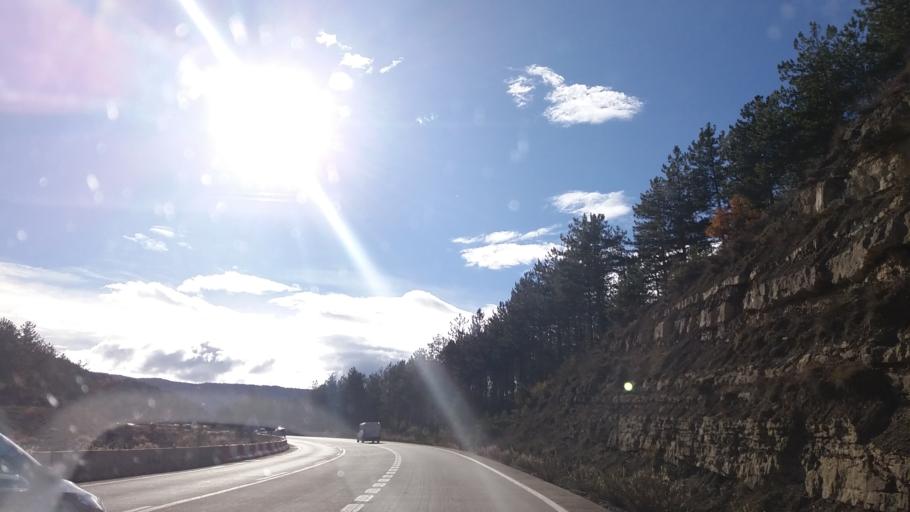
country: ES
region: Aragon
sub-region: Provincia de Huesca
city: Arguis
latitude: 42.3931
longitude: -0.3721
